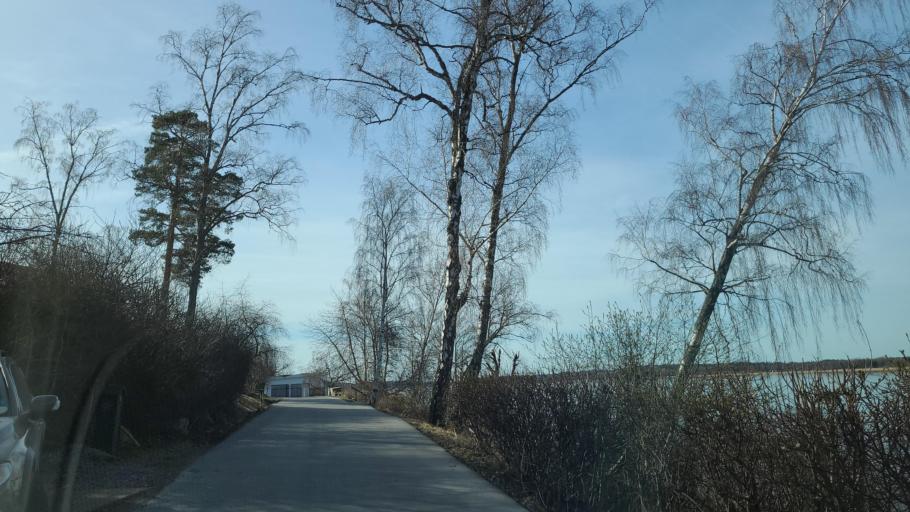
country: SE
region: Stockholm
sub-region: Ekero Kommun
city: Ekeroe
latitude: 59.2905
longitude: 17.7616
